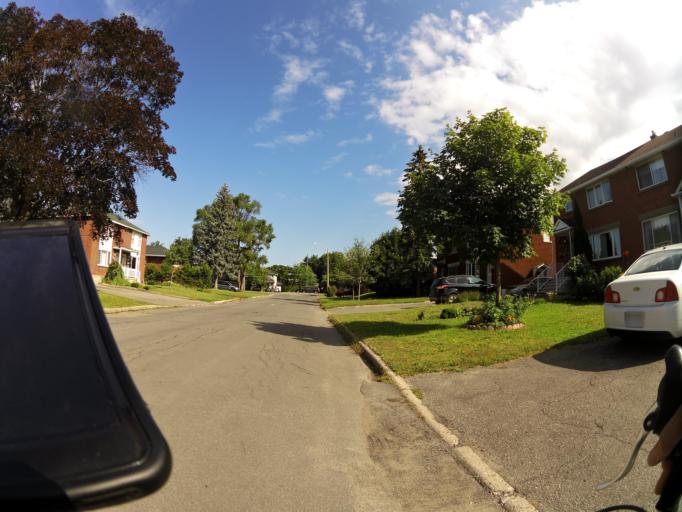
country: CA
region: Ontario
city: Ottawa
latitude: 45.3774
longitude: -75.6724
